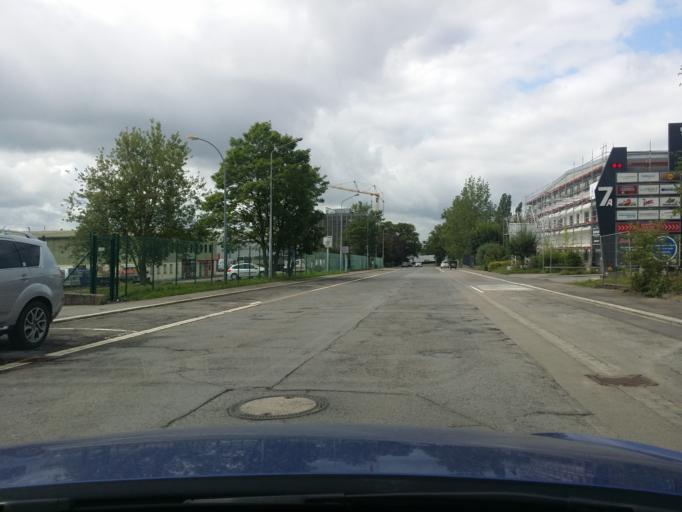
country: LU
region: Luxembourg
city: Kirchberg
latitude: 49.6127
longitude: 6.1688
